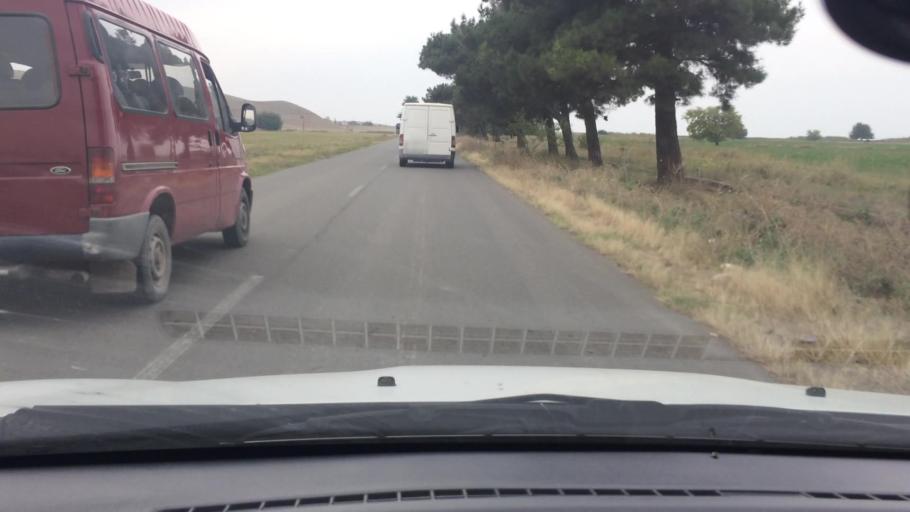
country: AM
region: Tavush
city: Berdavan
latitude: 41.3357
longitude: 45.0246
